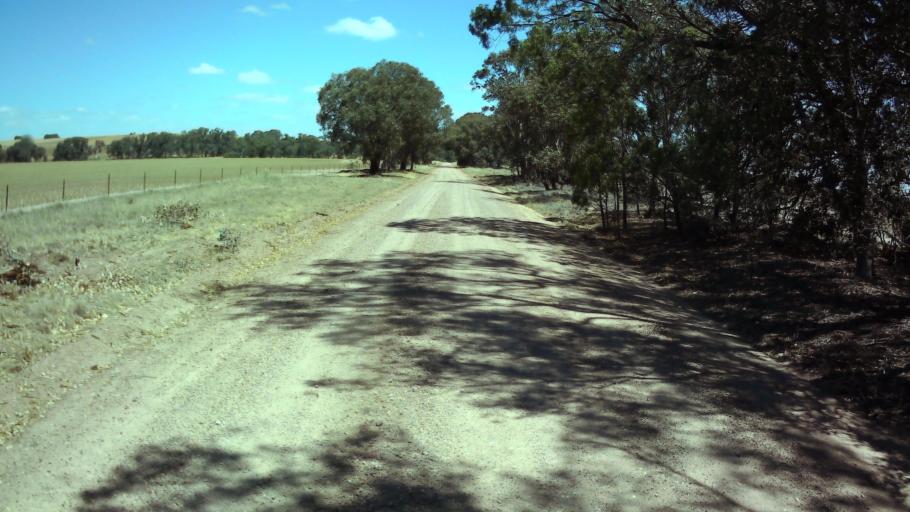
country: AU
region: New South Wales
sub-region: Weddin
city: Grenfell
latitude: -33.9274
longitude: 148.3351
